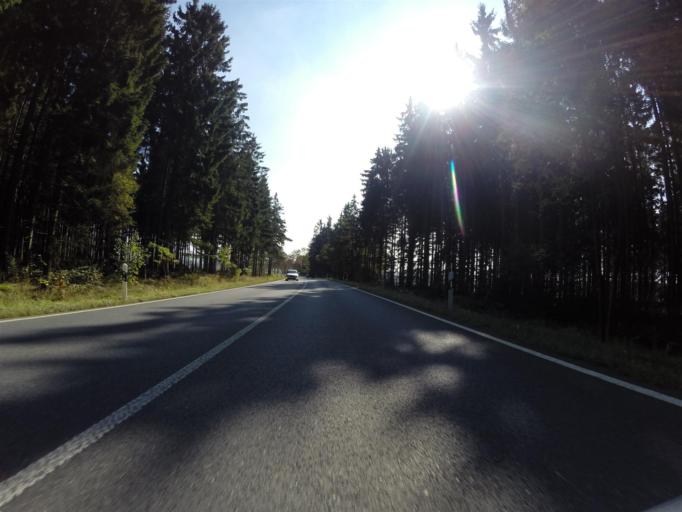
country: DE
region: Thuringia
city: Tanna
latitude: 50.4564
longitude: 11.8536
